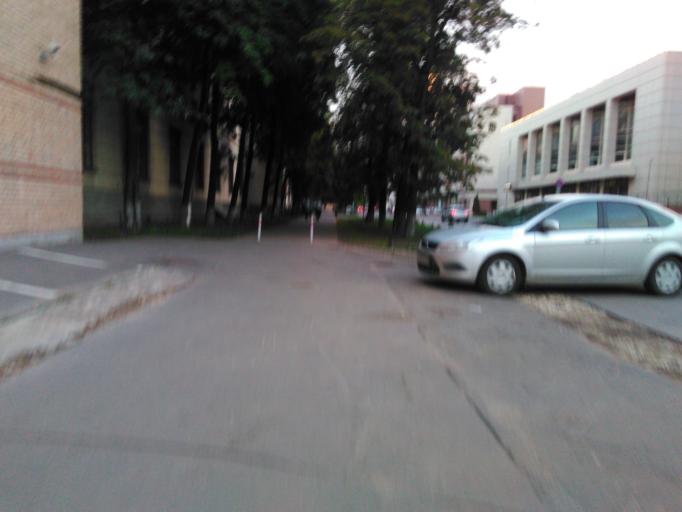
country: RU
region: Moscow
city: Novyye Cheremushki
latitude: 55.7082
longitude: 37.5994
